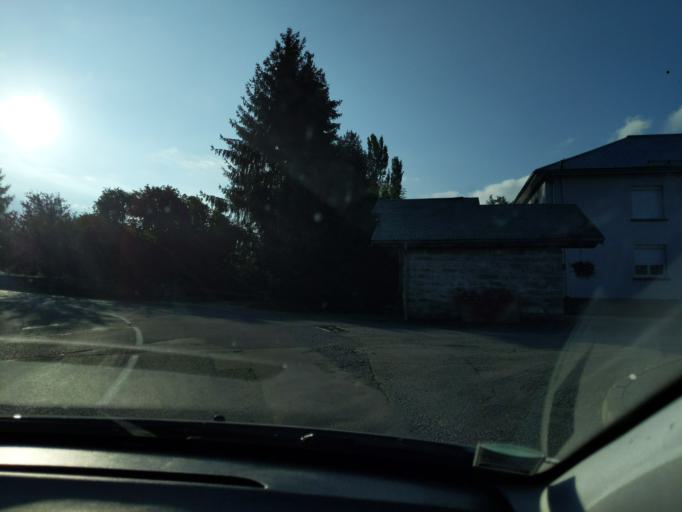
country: FR
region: Rhone-Alpes
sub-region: Departement de la Savoie
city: Aiton
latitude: 45.5601
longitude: 6.2553
